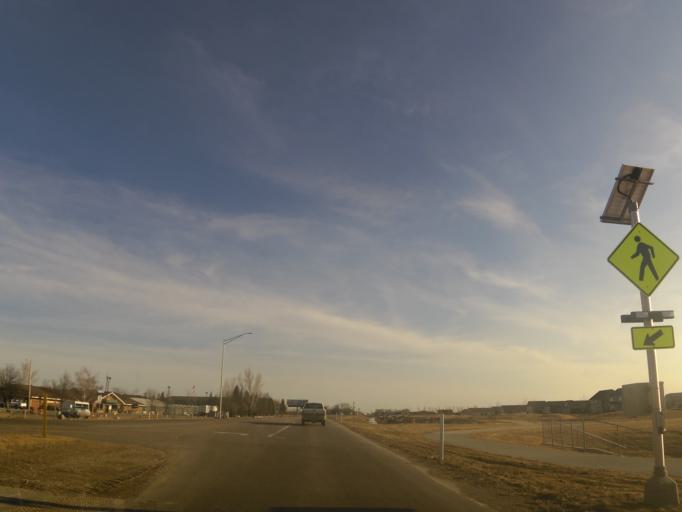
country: US
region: North Dakota
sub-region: Grand Forks County
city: Grand Forks
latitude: 47.8718
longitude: -97.0456
